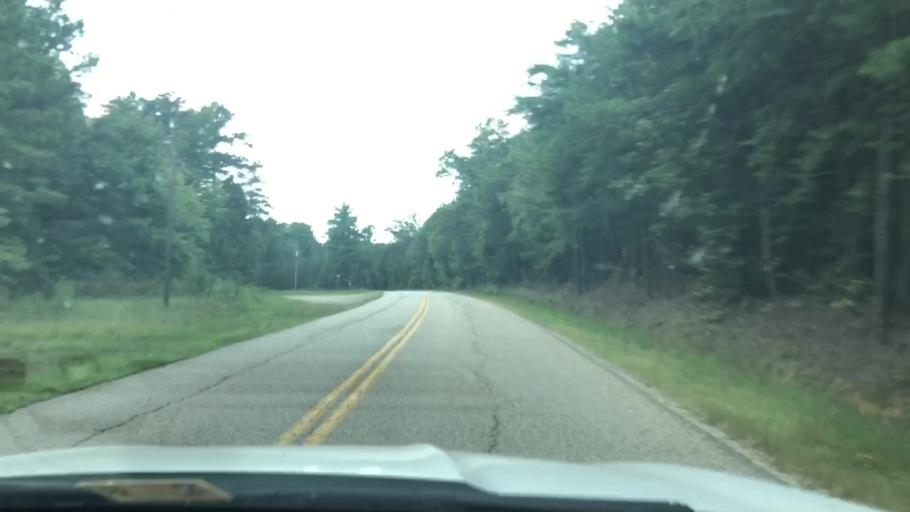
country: US
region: Virginia
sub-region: King William County
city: West Point
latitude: 37.6092
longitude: -76.7175
